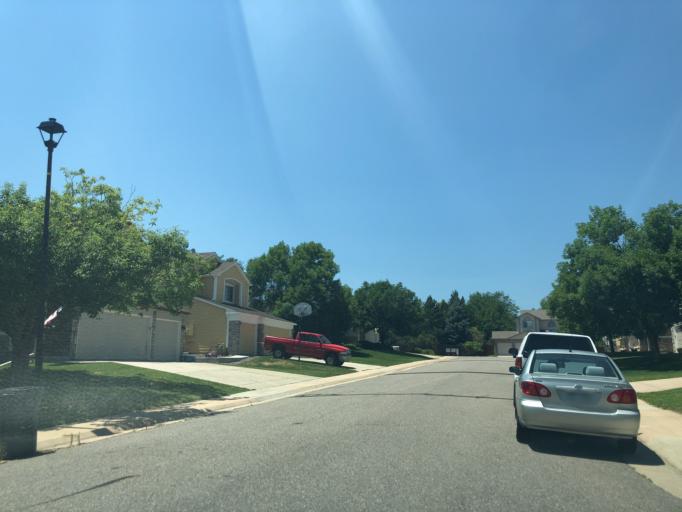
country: US
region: Colorado
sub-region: Arapahoe County
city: Dove Valley
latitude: 39.6213
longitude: -104.7549
